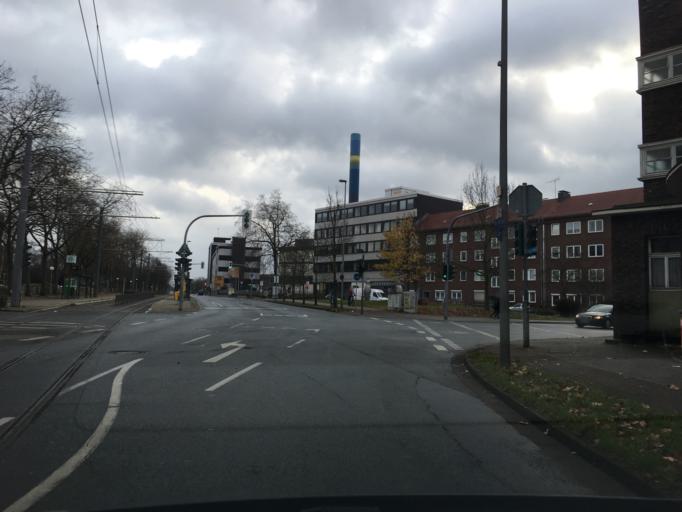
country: DE
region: North Rhine-Westphalia
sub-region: Regierungsbezirk Dusseldorf
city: Oberhausen
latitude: 51.4721
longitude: 6.8594
